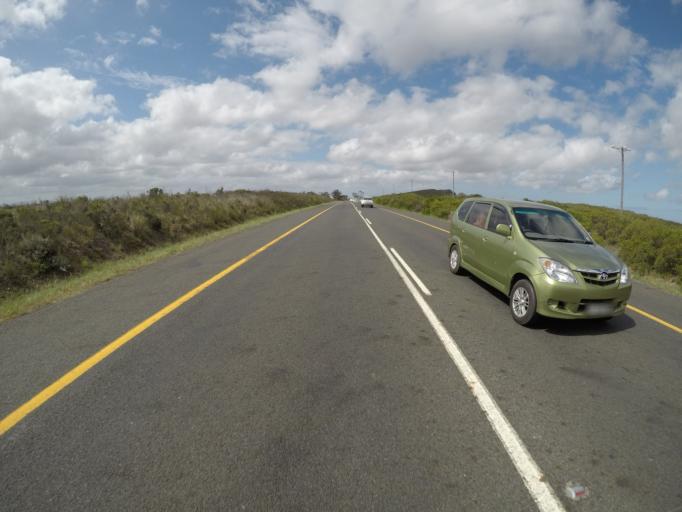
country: ZA
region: Western Cape
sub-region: Eden District Municipality
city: Mossel Bay
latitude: -34.1819
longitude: 21.8710
